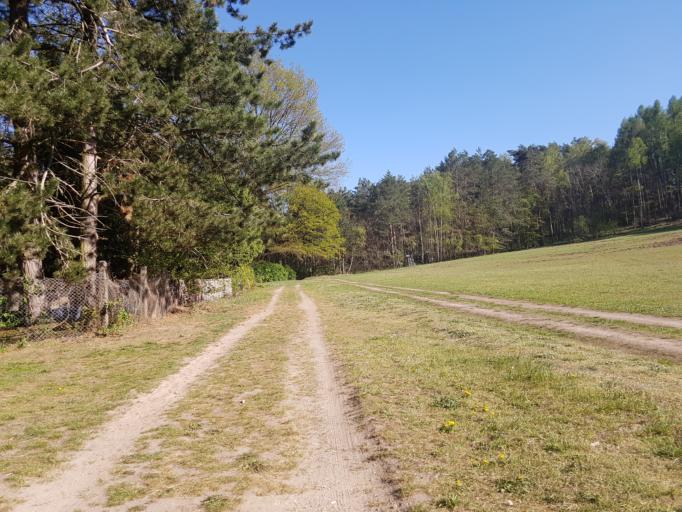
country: DE
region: Brandenburg
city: Groden
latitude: 51.3968
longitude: 13.5692
